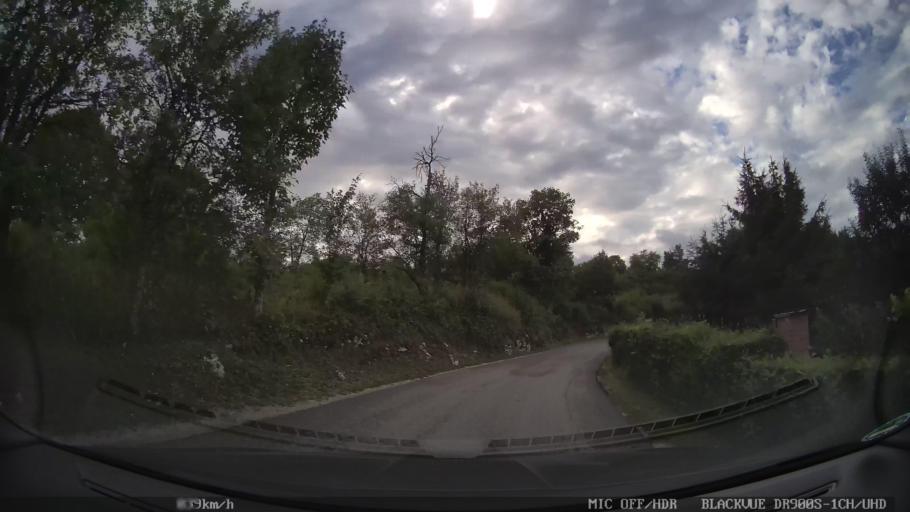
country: HR
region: Licko-Senjska
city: Jezerce
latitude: 44.9214
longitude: 15.5989
